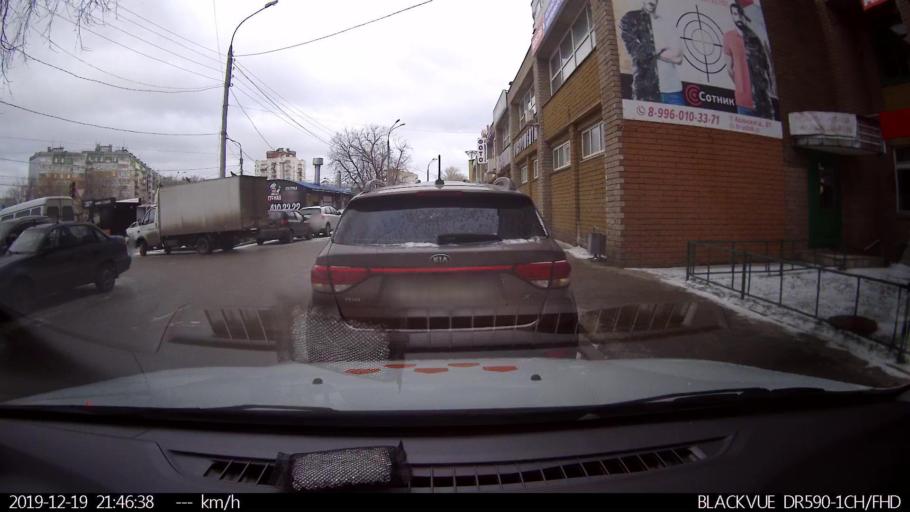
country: RU
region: Nizjnij Novgorod
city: Afonino
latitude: 56.2671
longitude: 44.0595
